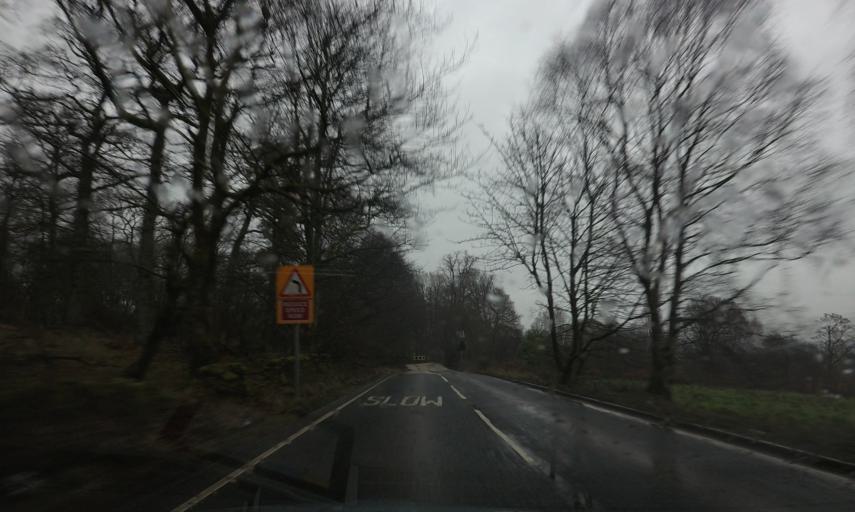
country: GB
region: Scotland
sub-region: East Dunbartonshire
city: Milngavie
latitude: 55.9388
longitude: -4.3482
